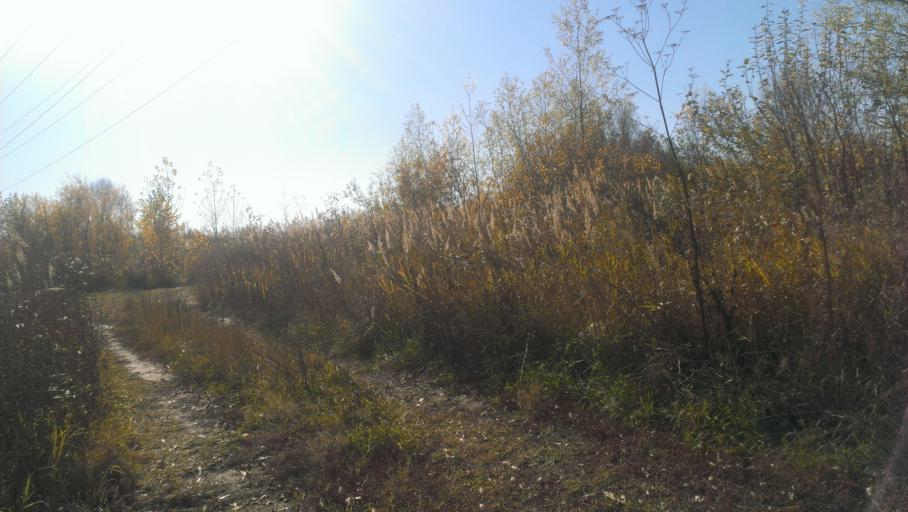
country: RU
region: Altai Krai
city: Novosilikatnyy
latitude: 53.3439
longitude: 83.6349
